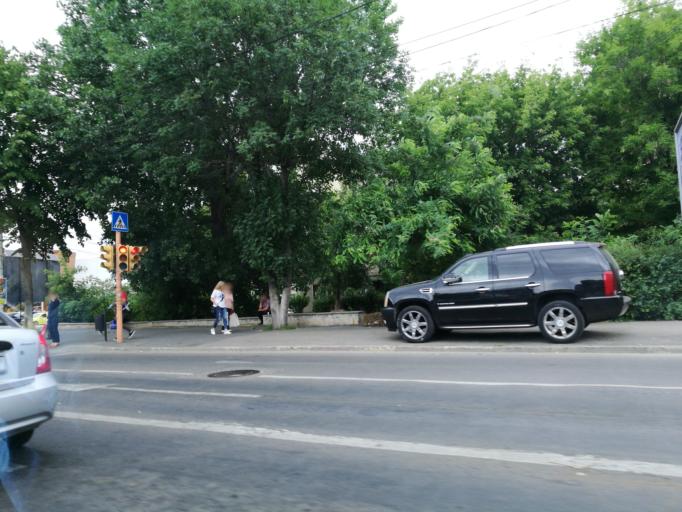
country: RO
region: Constanta
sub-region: Municipiul Constanta
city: Constanta
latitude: 44.2018
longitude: 28.6307
